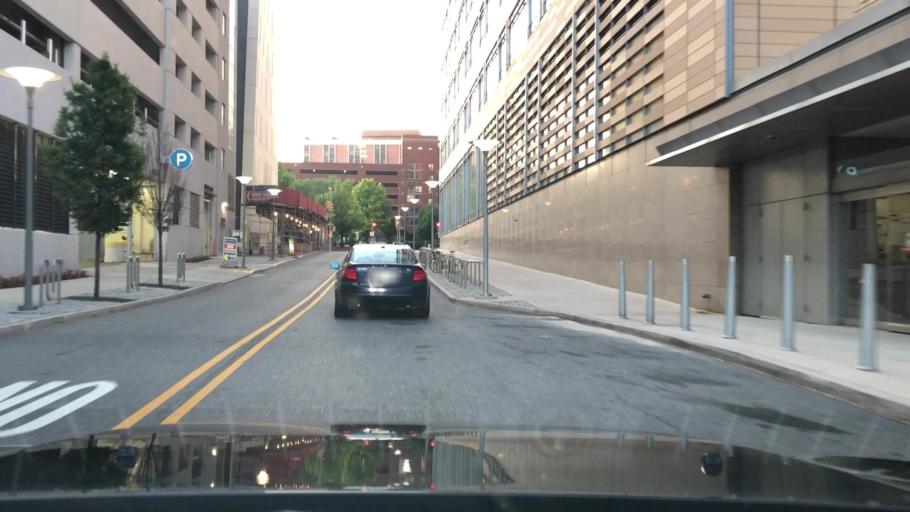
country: US
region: Pennsylvania
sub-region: Philadelphia County
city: Philadelphia
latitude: 39.9456
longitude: -75.1951
